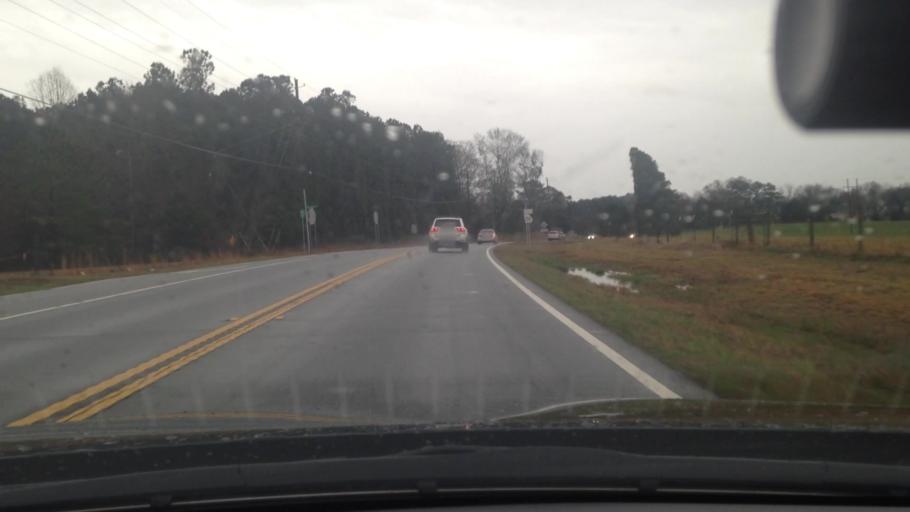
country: US
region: Georgia
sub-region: Fayette County
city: Peachtree City
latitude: 33.3775
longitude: -84.6685
